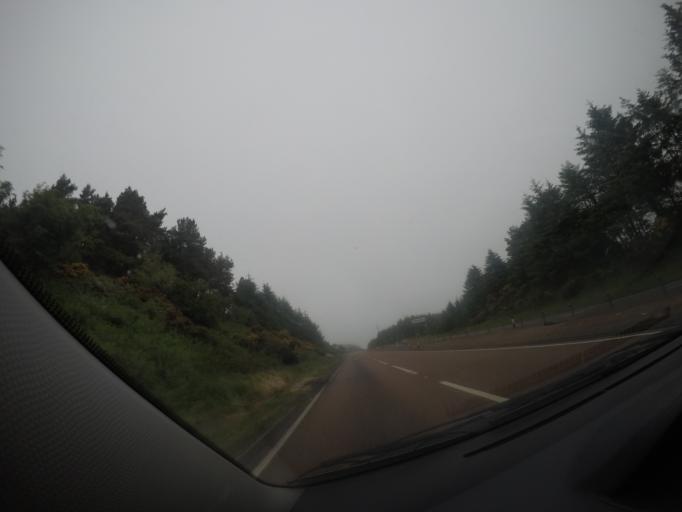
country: GB
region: Scotland
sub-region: Dundee City
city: Dundee
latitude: 56.5461
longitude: -2.9414
